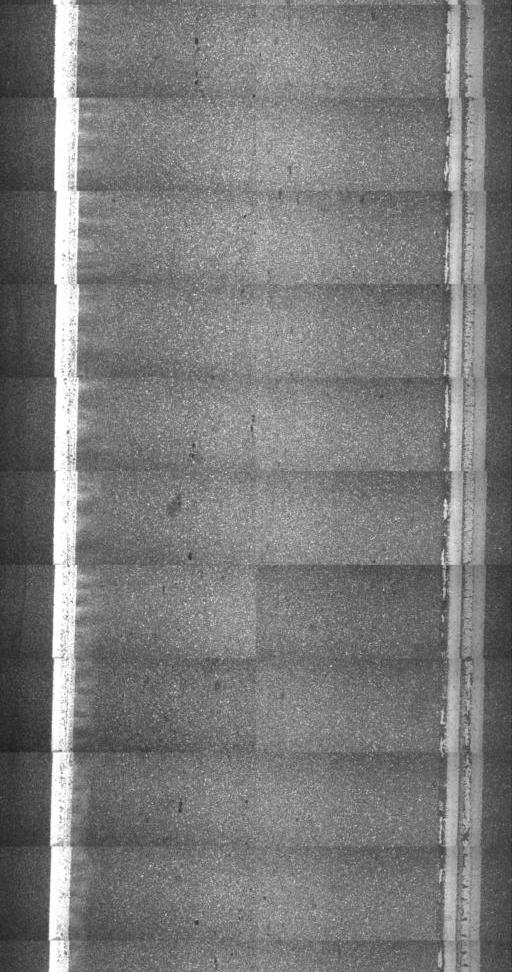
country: US
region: New Hampshire
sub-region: Grafton County
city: Orford
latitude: 43.8877
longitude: -72.2401
